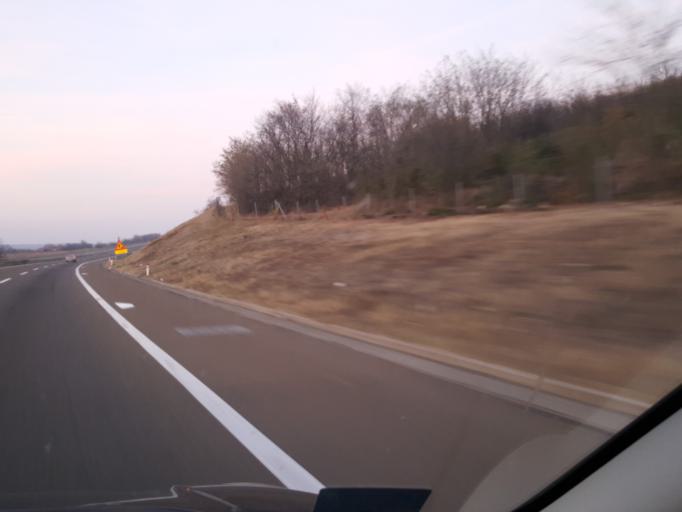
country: RS
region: Central Serbia
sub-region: Pomoravski Okrug
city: Paracin
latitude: 43.8346
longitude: 21.4275
